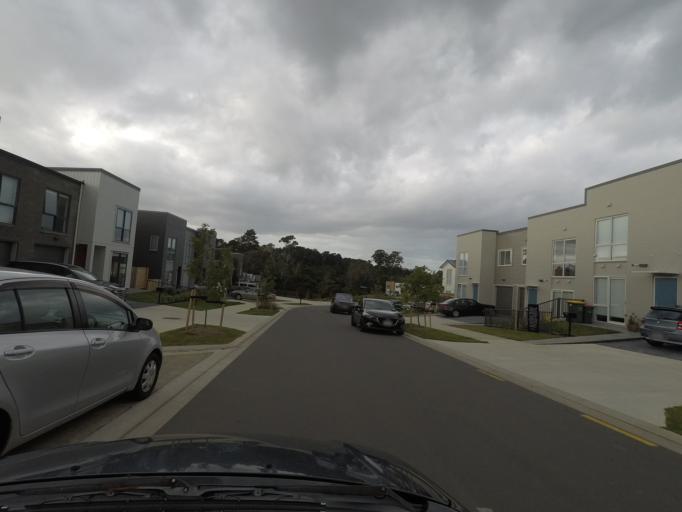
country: NZ
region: Auckland
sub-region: Auckland
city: Rosebank
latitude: -36.8266
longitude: 174.6266
